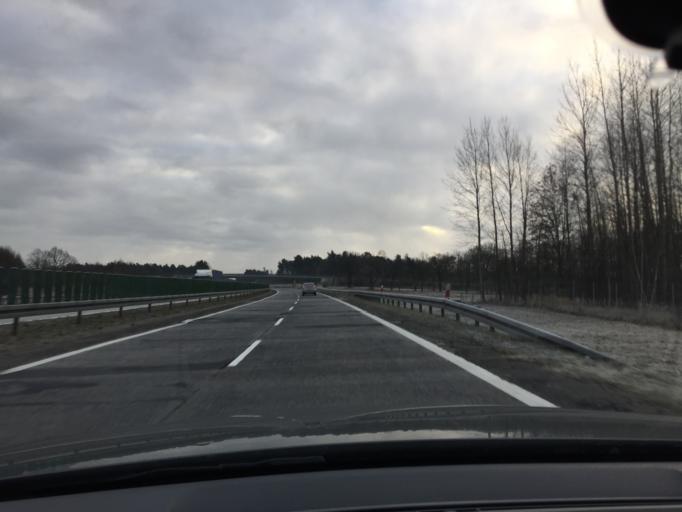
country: PL
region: Lubusz
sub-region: Powiat zarski
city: Lipinki Luzyckie
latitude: 51.5951
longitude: 14.9998
